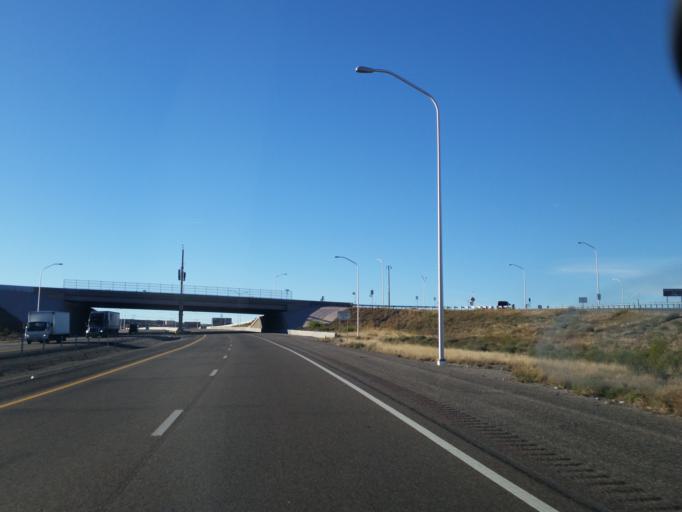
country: US
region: New Mexico
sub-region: Sandoval County
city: Bernalillo
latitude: 35.3181
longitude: -106.5335
